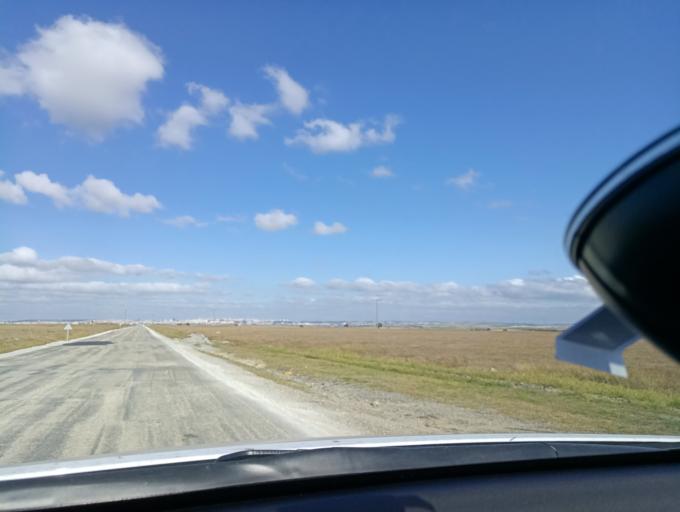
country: TR
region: Tekirdag
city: Corlu
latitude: 41.0670
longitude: 27.8337
